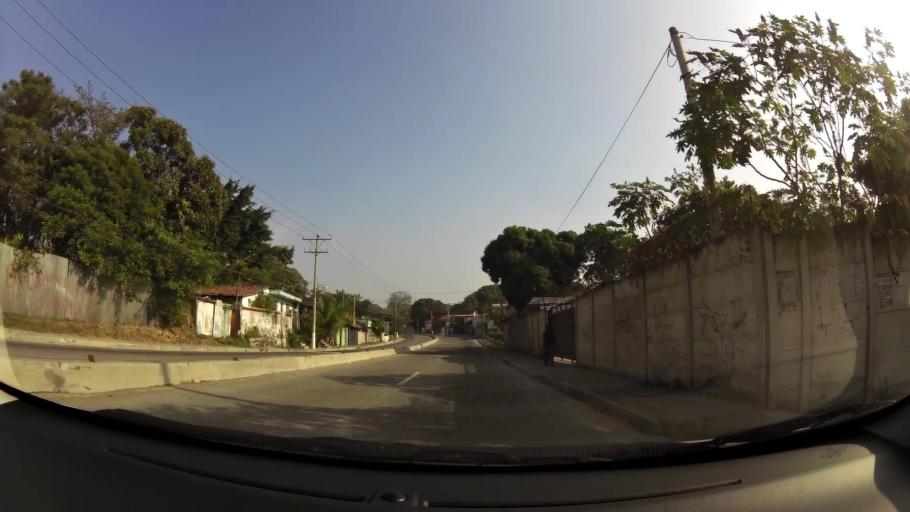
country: SV
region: La Libertad
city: Antiguo Cuscatlan
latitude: 13.6698
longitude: -89.2230
